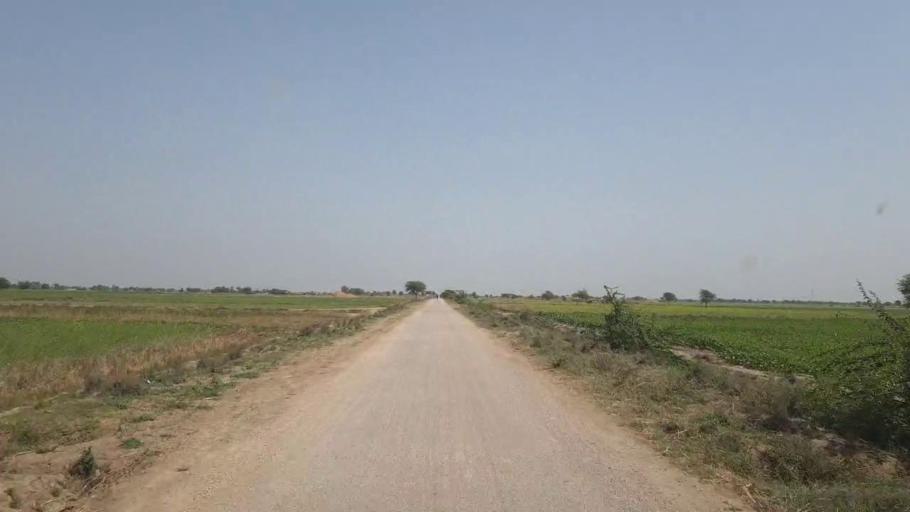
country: PK
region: Sindh
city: Jati
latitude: 24.4774
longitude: 68.5571
